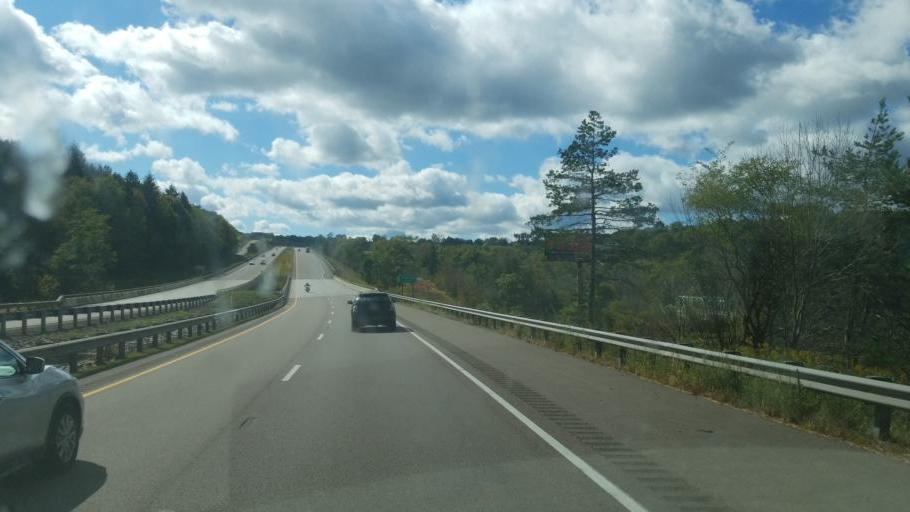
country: US
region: Pennsylvania
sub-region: Somerset County
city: Meyersdale
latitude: 39.6955
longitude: -79.1383
